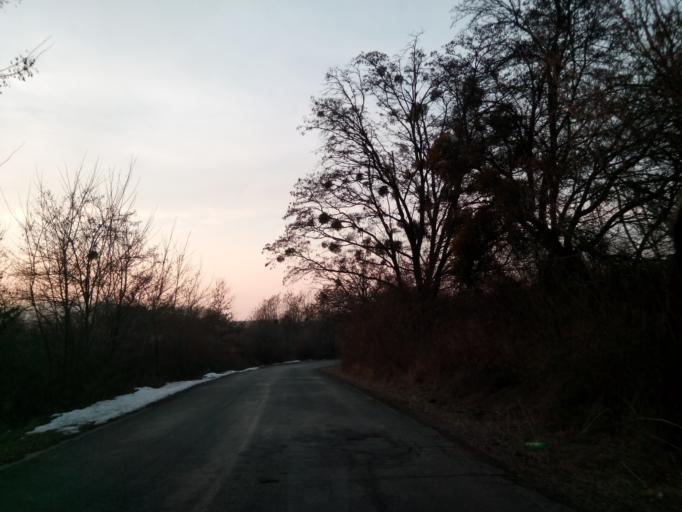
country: HU
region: Borsod-Abauj-Zemplen
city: Gonc
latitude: 48.4872
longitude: 21.3844
